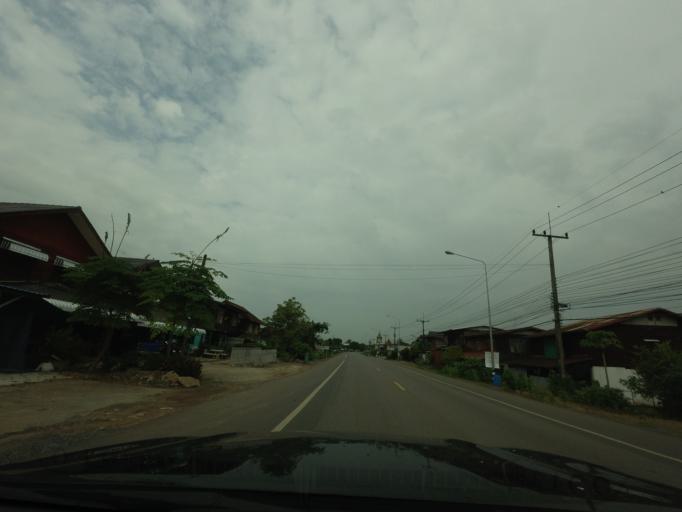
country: TH
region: Nong Khai
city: Tha Bo
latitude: 17.7997
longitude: 102.6700
